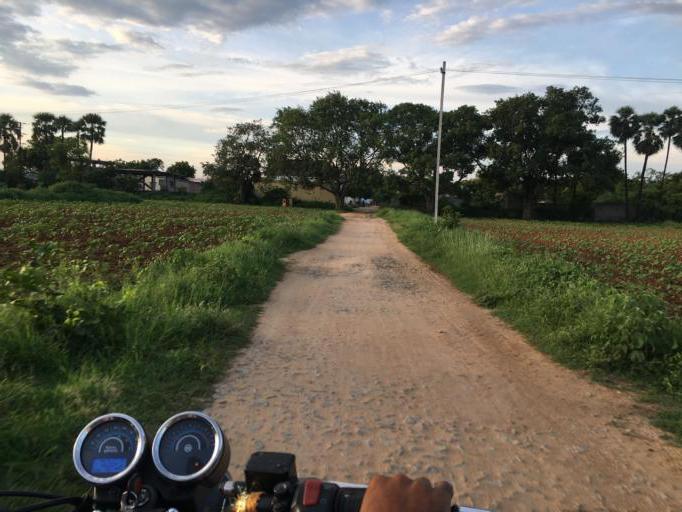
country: IN
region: Telangana
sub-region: Nalgonda
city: Nalgonda
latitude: 17.1723
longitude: 79.4175
